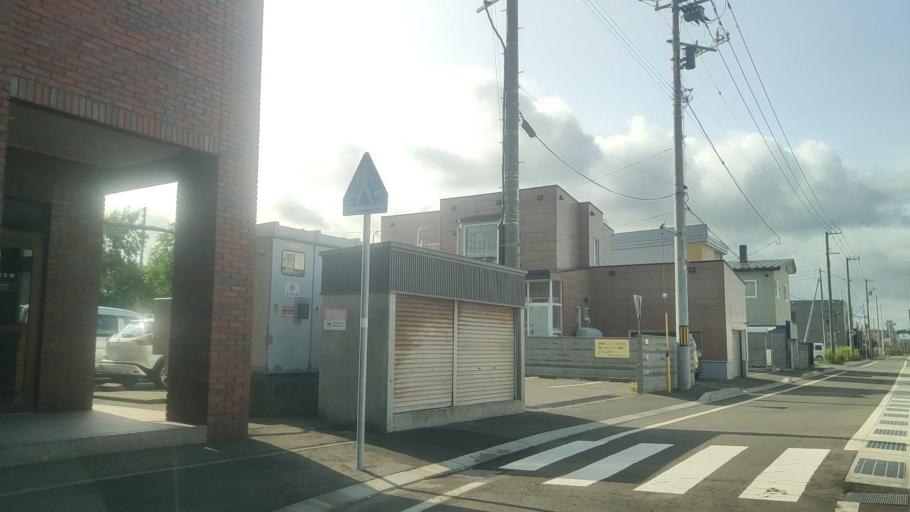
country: JP
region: Hokkaido
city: Tomakomai
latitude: 42.6416
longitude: 141.6097
